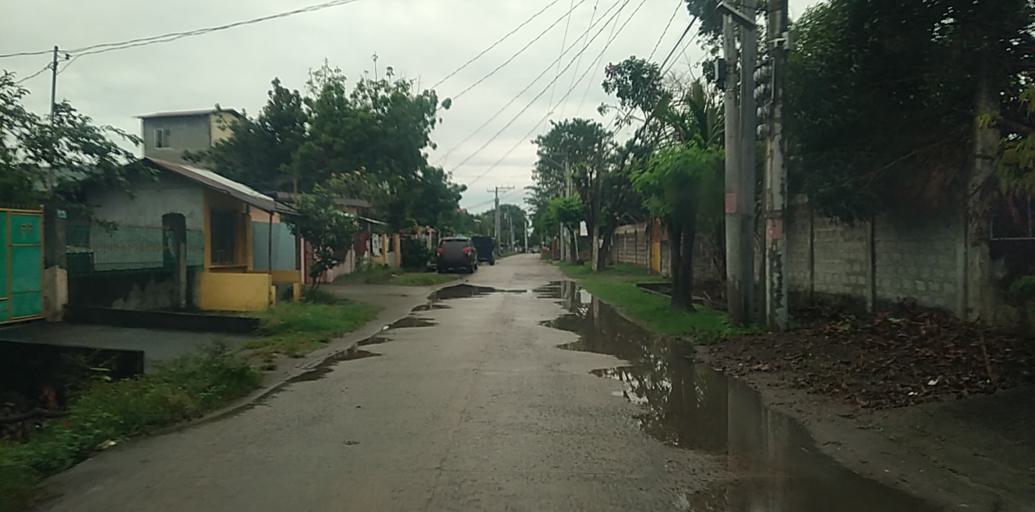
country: PH
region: Central Luzon
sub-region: Province of Pampanga
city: Arayat
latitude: 15.1475
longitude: 120.7413
